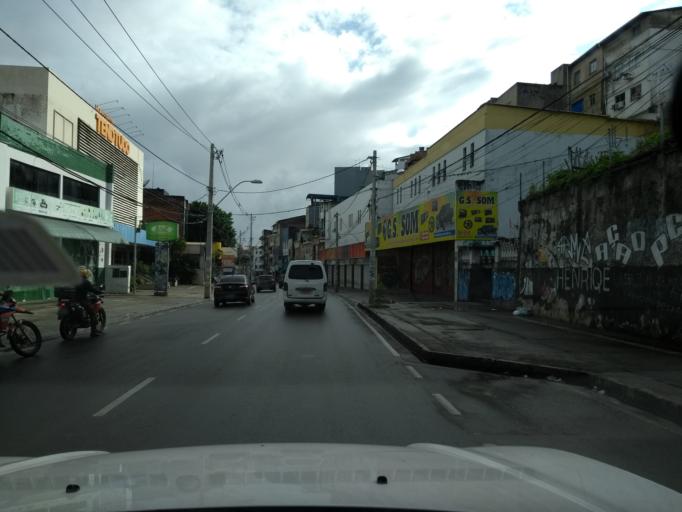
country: BR
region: Bahia
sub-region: Salvador
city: Salvador
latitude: -12.9752
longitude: -38.5002
